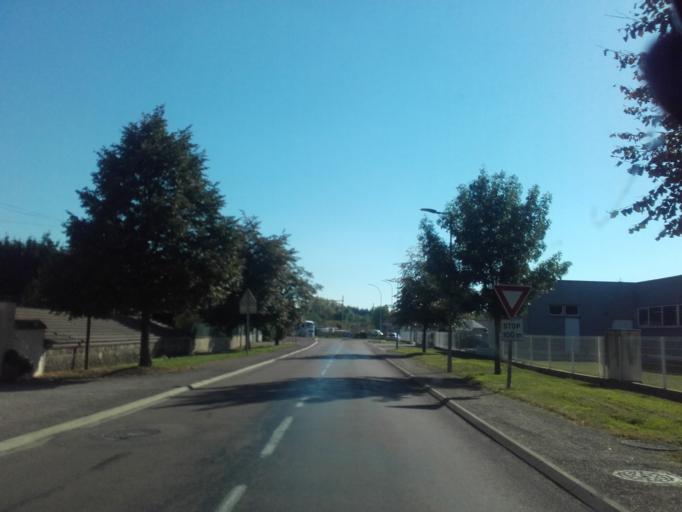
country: FR
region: Bourgogne
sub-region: Departement de la Cote-d'Or
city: Corpeau
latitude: 46.9197
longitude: 4.7529
